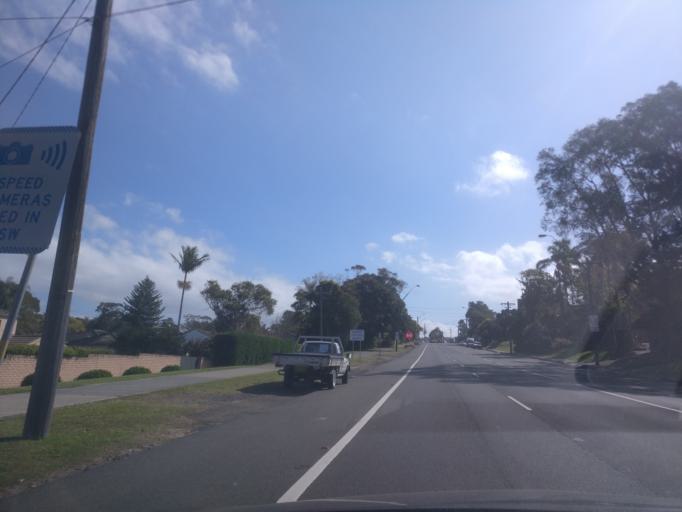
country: AU
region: New South Wales
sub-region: Pittwater
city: Warriewood
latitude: -33.6781
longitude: 151.2977
